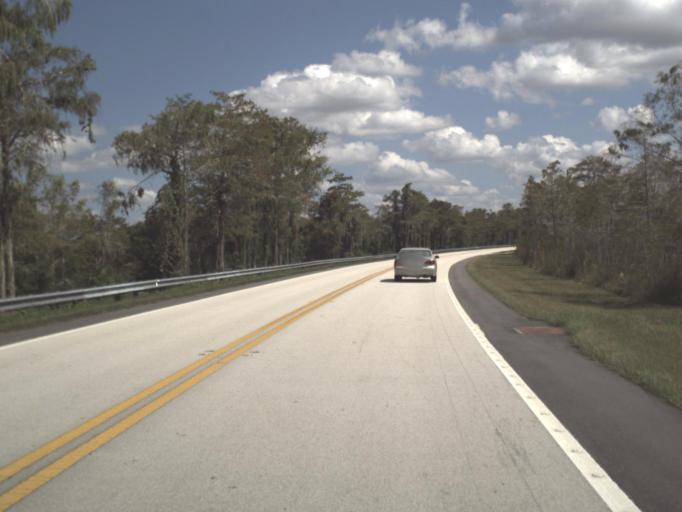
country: US
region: Florida
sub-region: Miami-Dade County
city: Kendall West
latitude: 25.8455
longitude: -80.9214
